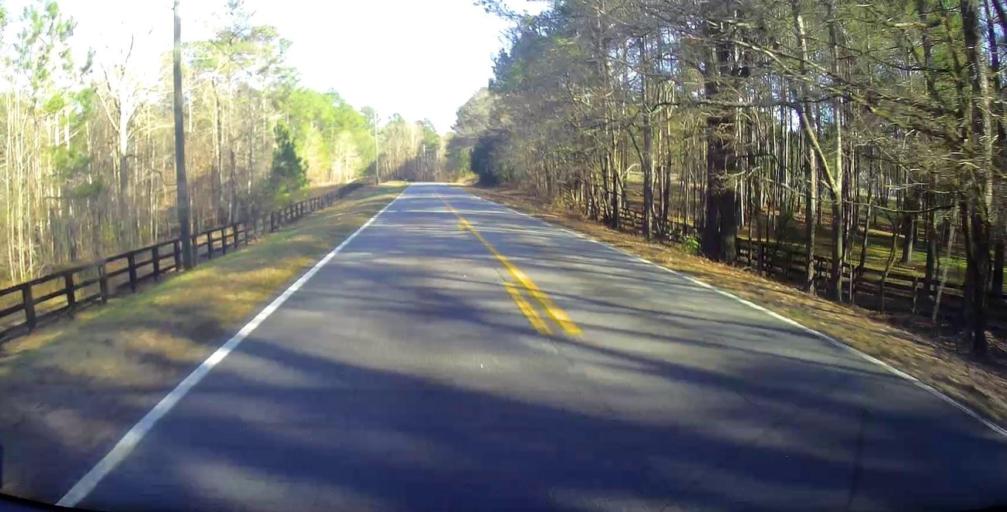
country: US
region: Georgia
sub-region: Harris County
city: Hamilton
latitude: 32.5594
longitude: -84.7840
